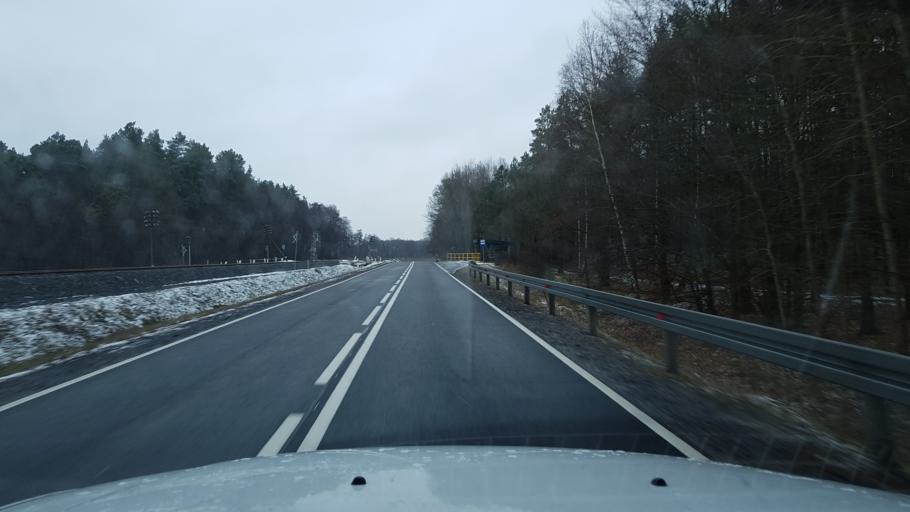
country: PL
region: West Pomeranian Voivodeship
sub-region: Powiat szczecinecki
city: Lubowo
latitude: 53.6139
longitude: 16.4469
